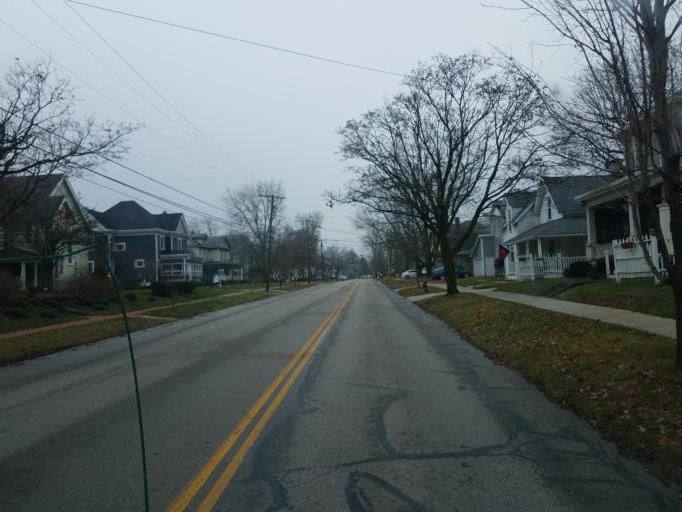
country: US
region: Ohio
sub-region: Union County
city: Marysville
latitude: 40.2369
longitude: -83.3735
